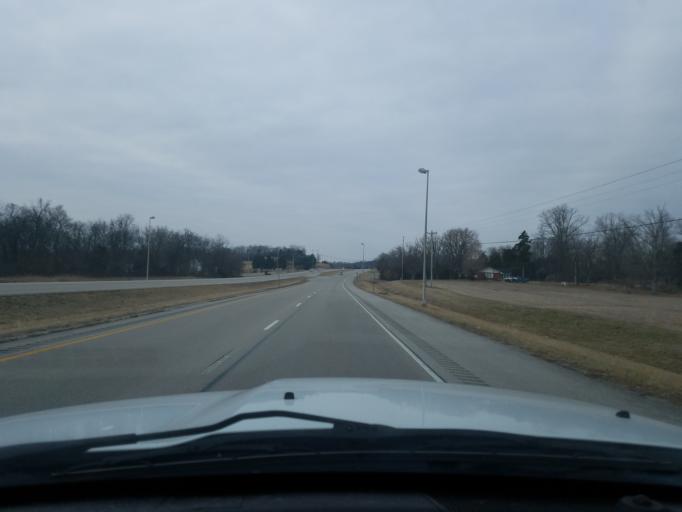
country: US
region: Kentucky
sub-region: Warren County
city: Bowling Green
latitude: 36.9406
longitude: -86.5306
